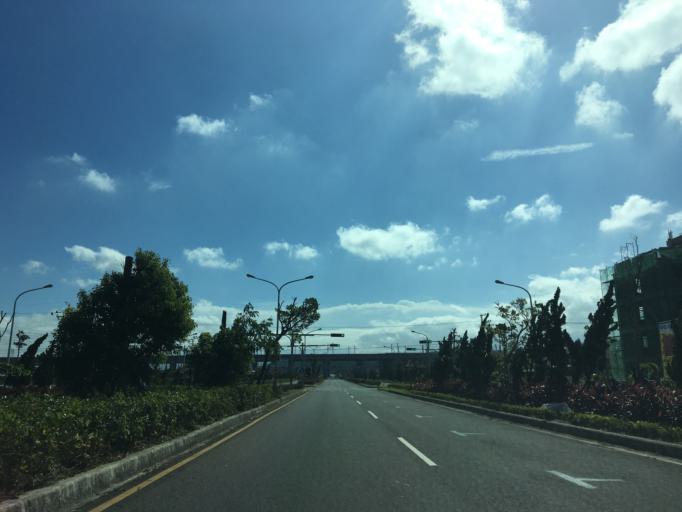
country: TW
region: Taiwan
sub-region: Hsinchu
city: Zhubei
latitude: 24.7876
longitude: 121.0307
